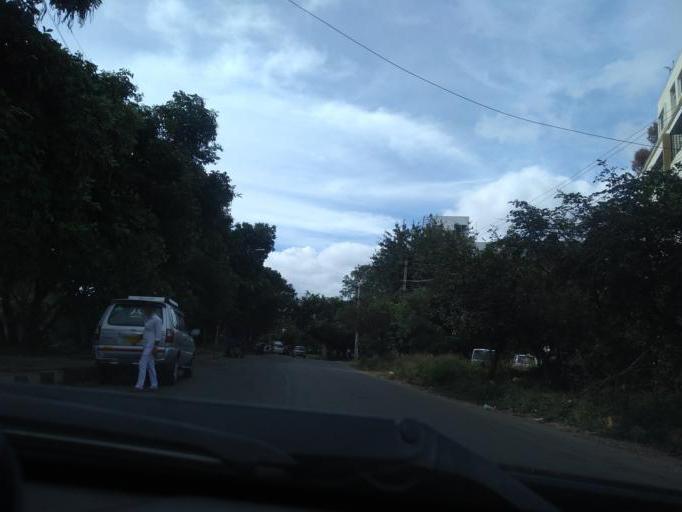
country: IN
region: Karnataka
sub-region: Bangalore Urban
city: Bangalore
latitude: 13.0030
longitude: 77.6585
